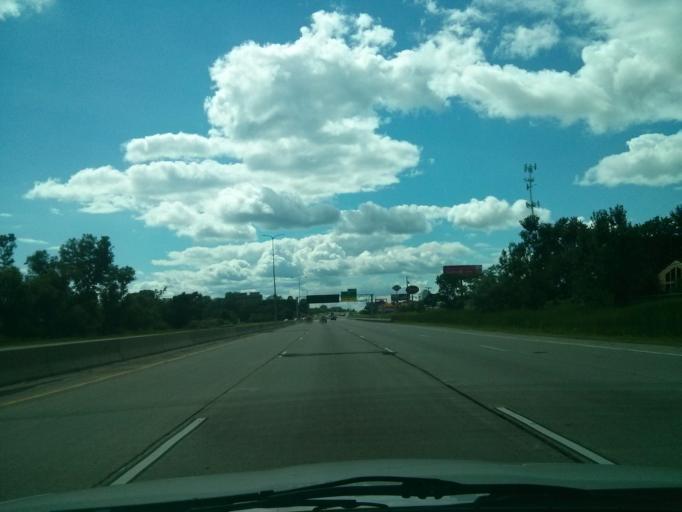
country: US
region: Minnesota
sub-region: Washington County
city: Oakdale
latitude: 44.9487
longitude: -92.9707
